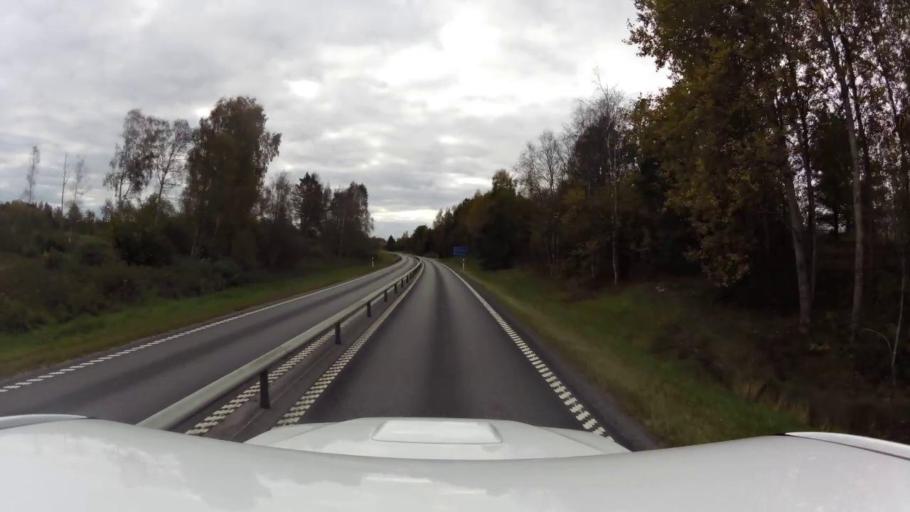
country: SE
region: OEstergoetland
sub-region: Linkopings Kommun
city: Malmslatt
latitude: 58.2923
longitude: 15.5649
